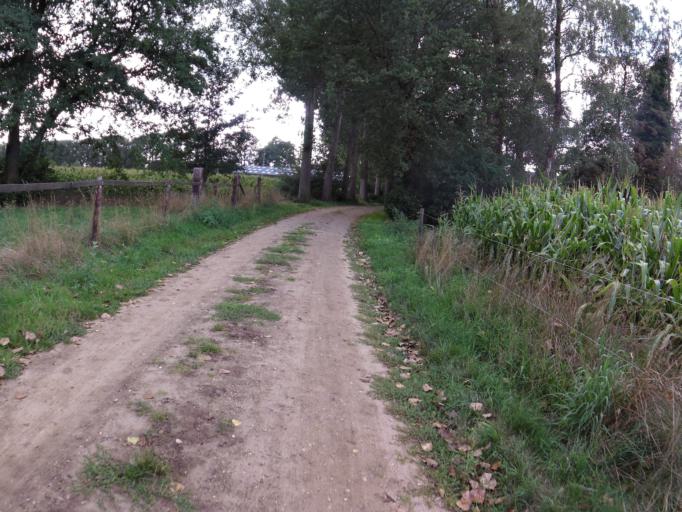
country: NL
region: Gelderland
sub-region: Gemeente Aalten
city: Aalten
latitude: 51.9317
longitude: 6.5990
